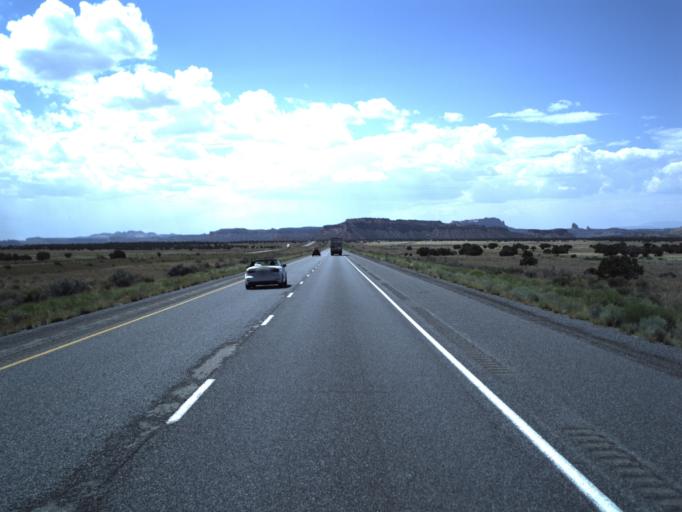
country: US
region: Utah
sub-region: Emery County
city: Castle Dale
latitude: 38.8954
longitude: -110.6124
